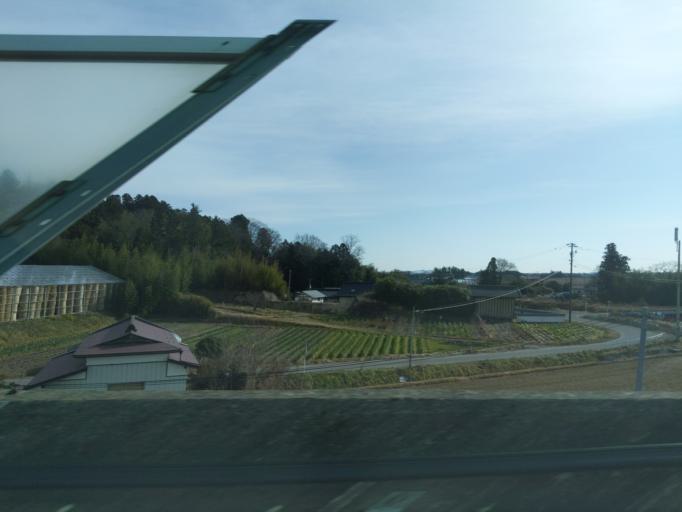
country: JP
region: Miyagi
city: Furukawa
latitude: 38.6147
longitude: 140.9929
